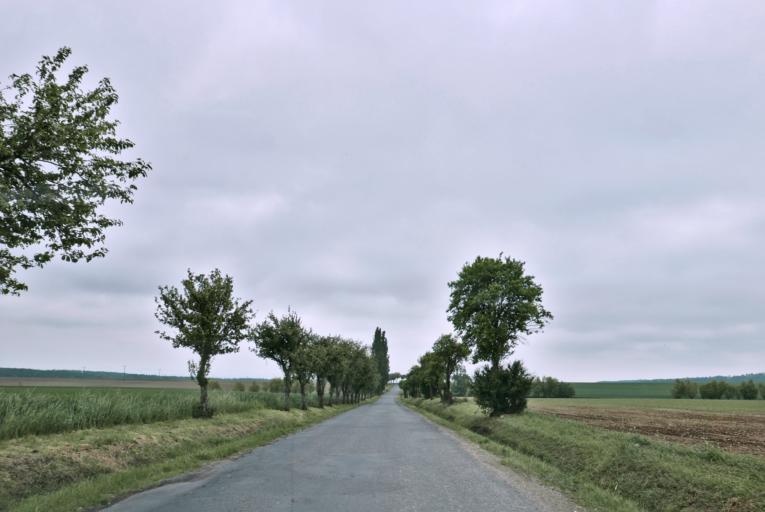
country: CZ
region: Plzensky
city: Kralovice
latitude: 49.9577
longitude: 13.4629
